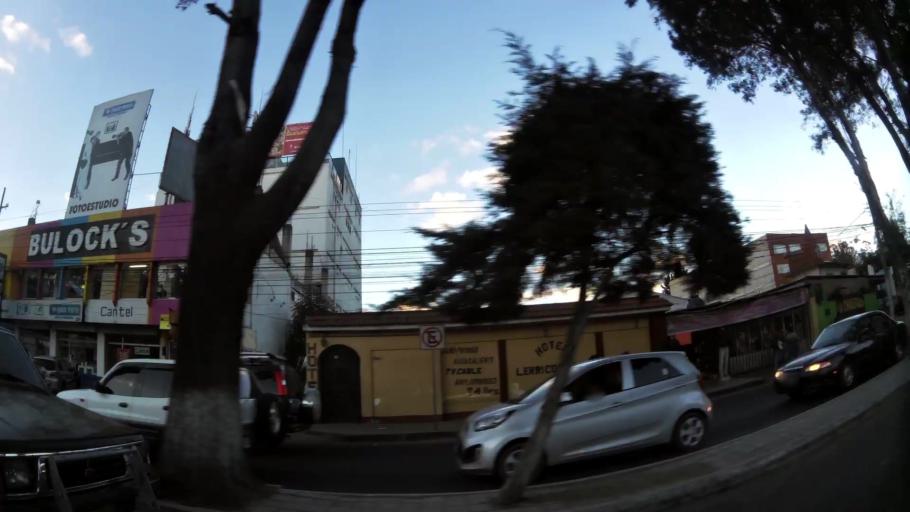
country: GT
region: Quetzaltenango
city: Quetzaltenango
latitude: 14.8441
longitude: -91.5187
